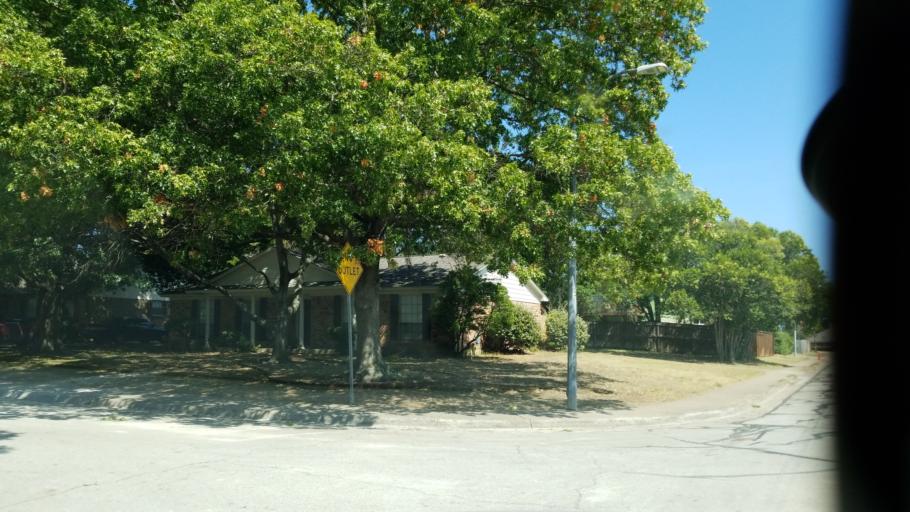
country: US
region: Texas
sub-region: Dallas County
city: Duncanville
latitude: 32.6461
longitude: -96.8961
